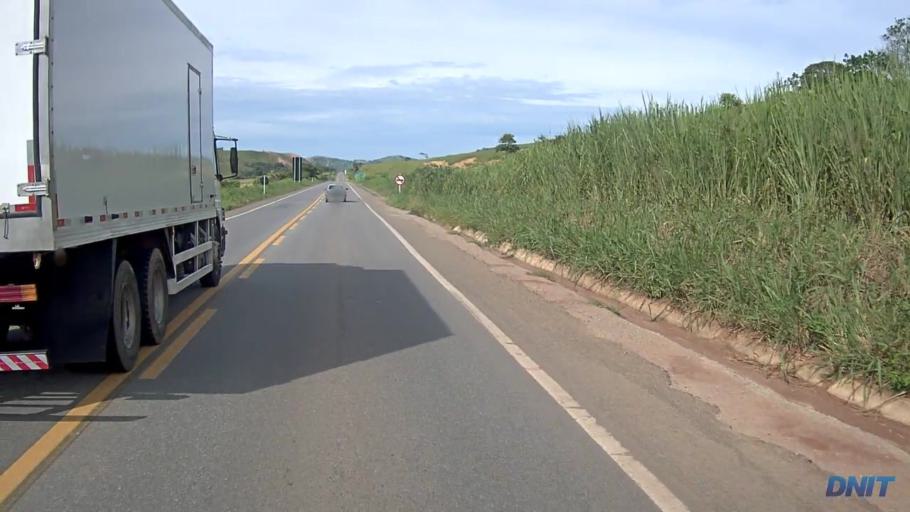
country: BR
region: Minas Gerais
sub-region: Belo Oriente
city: Belo Oriente
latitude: -19.1960
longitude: -42.2817
